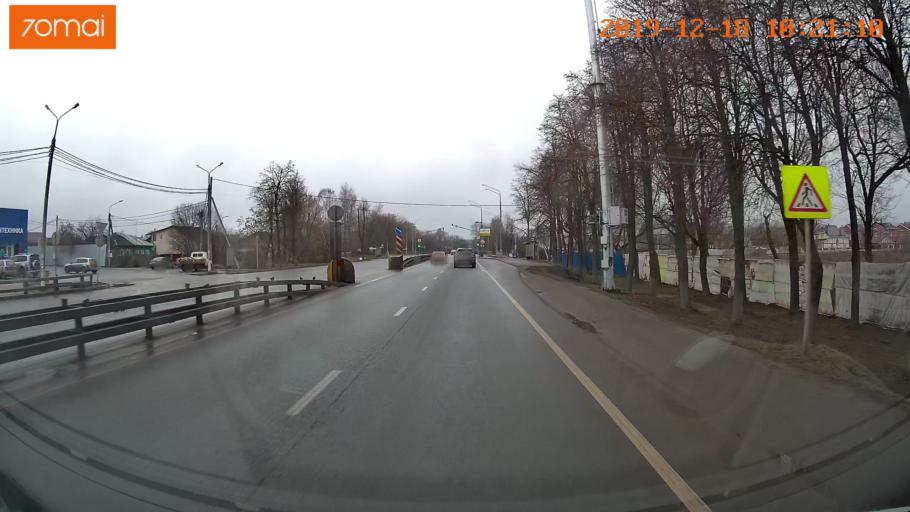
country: RU
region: Moskovskaya
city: Dubrovitsy
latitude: 55.3890
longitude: 37.4220
